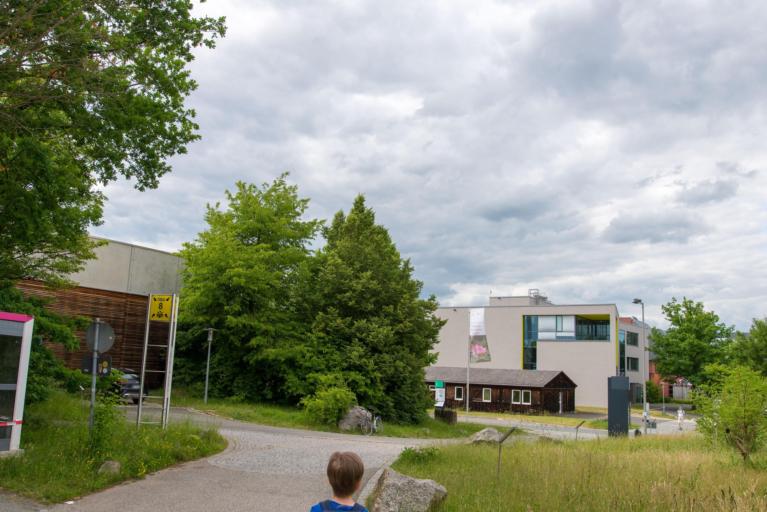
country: DE
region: Bavaria
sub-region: Upper Franconia
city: Bayreuth
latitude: 49.9264
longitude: 11.5853
